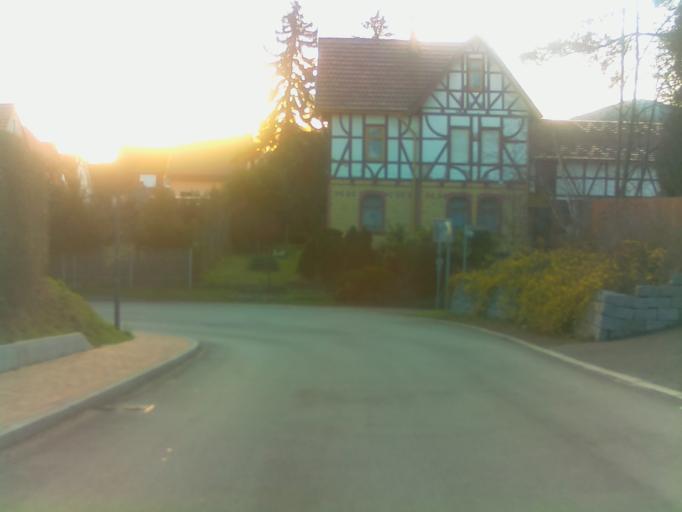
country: DE
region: Thuringia
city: Saalfeld
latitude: 50.6554
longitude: 11.3250
